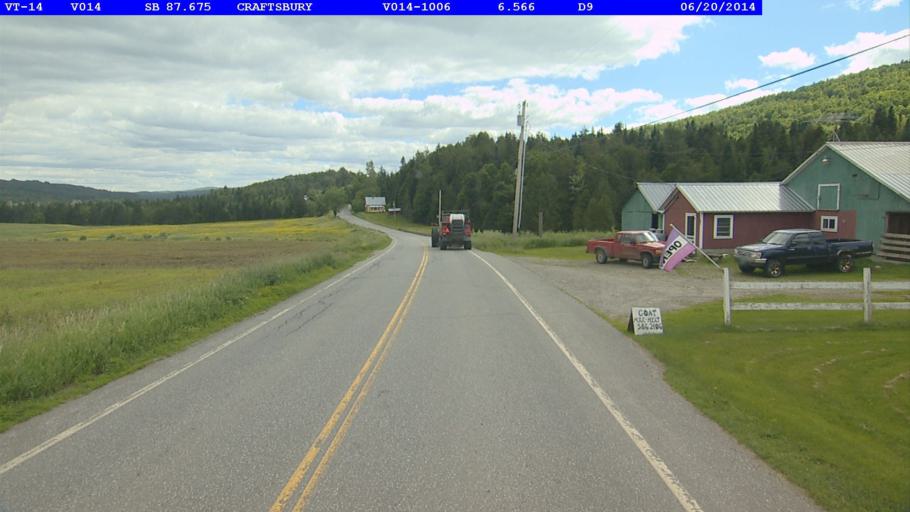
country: US
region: Vermont
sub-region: Caledonia County
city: Hardwick
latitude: 44.6849
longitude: -72.4030
